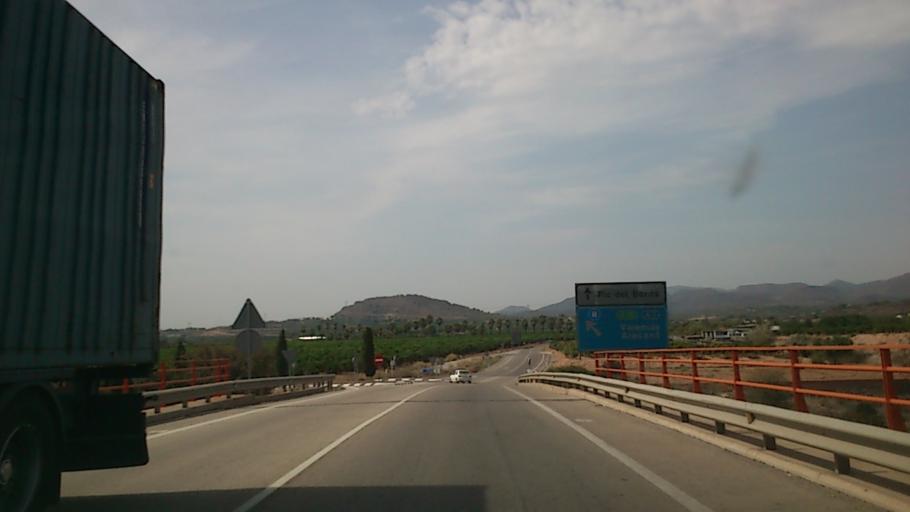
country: ES
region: Valencia
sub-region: Provincia de Valencia
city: Museros
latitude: 39.6095
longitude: -0.3450
